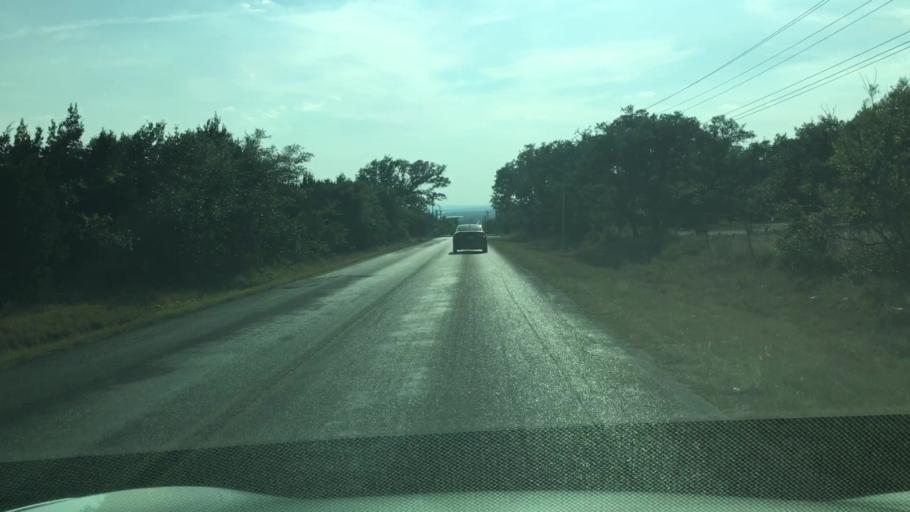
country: US
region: Texas
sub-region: Hays County
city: Dripping Springs
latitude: 30.1536
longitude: -98.0071
